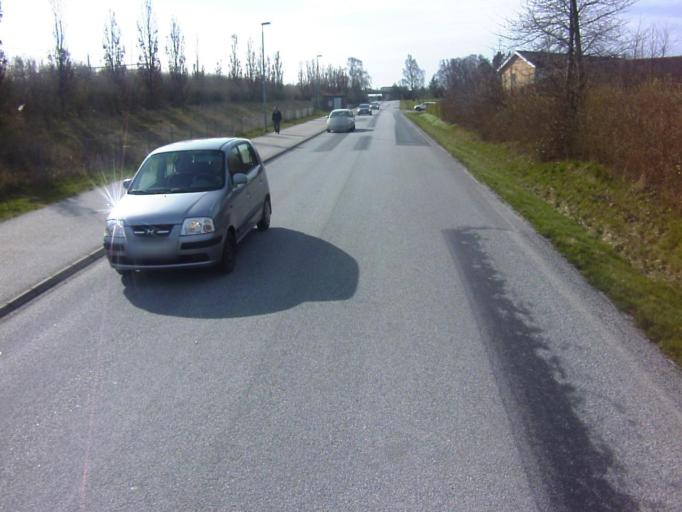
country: SE
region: Skane
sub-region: Kavlinge Kommun
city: Kaevlinge
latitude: 55.8002
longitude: 13.1097
